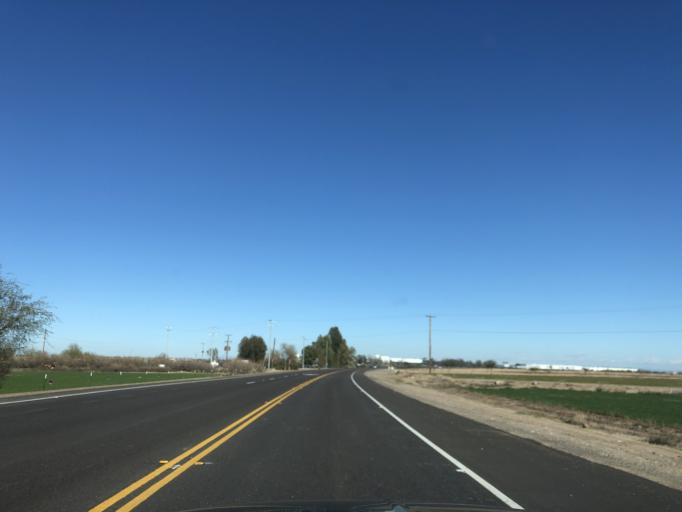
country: US
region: Arizona
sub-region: Maricopa County
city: Goodyear
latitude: 33.3985
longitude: -112.4403
